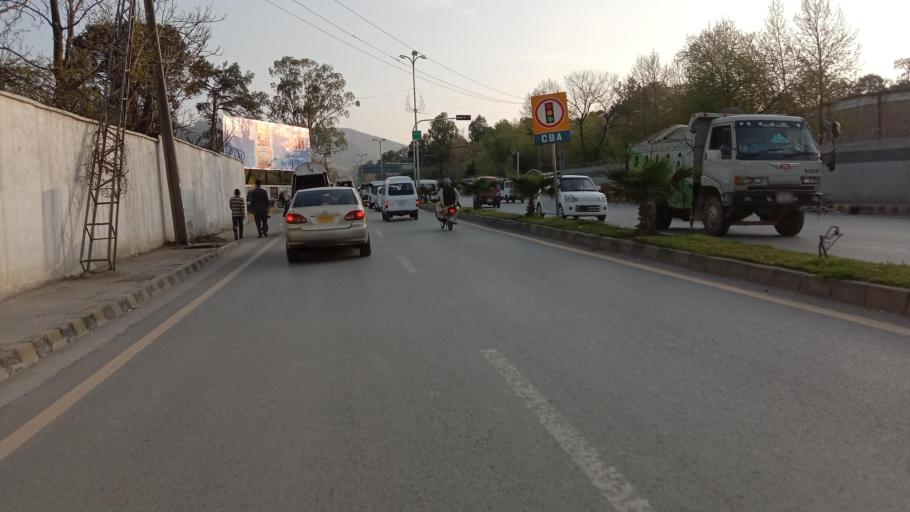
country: PK
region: Khyber Pakhtunkhwa
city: Abbottabad
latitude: 34.1652
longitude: 73.2234
